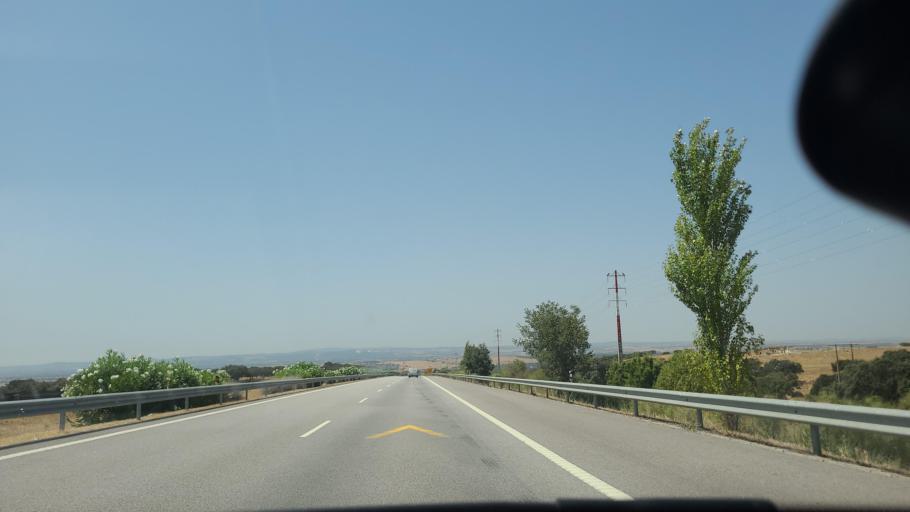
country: PT
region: Portalegre
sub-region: Elvas
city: Elvas
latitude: 38.8689
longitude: -7.2826
